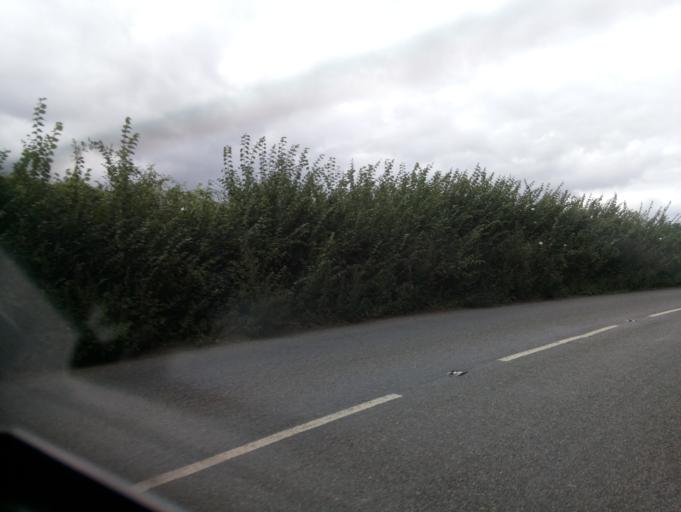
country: GB
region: England
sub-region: Devon
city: Starcross
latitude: 50.6360
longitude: -3.4594
